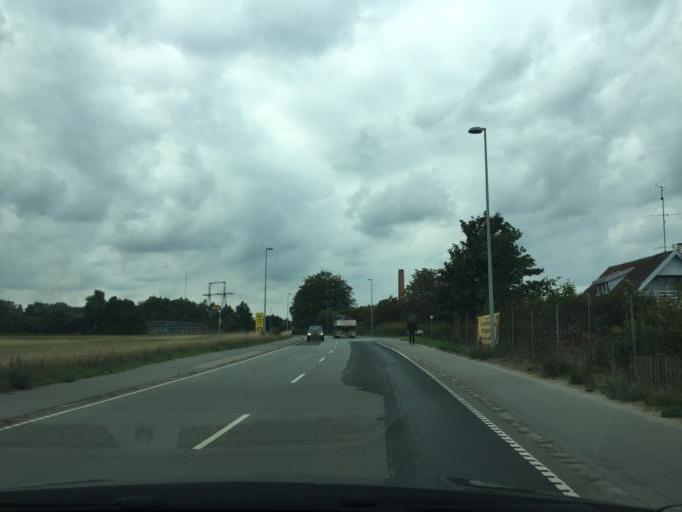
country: DK
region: South Denmark
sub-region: Odense Kommune
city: Stige
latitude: 55.4383
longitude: 10.3925
